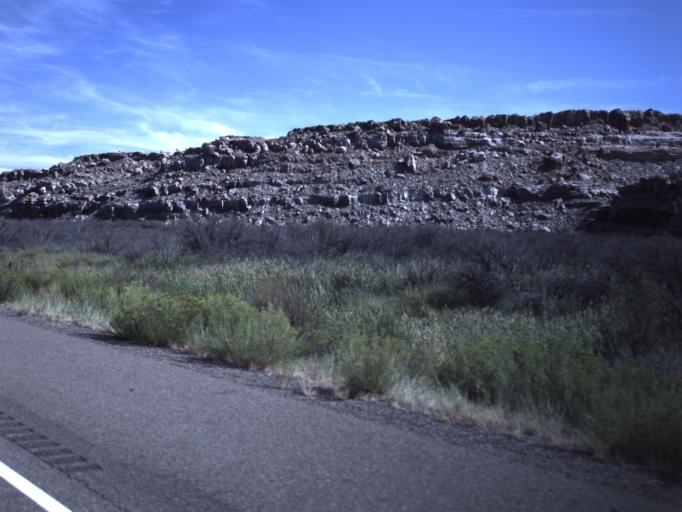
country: US
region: Utah
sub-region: Carbon County
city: East Carbon City
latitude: 38.9225
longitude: -110.4017
